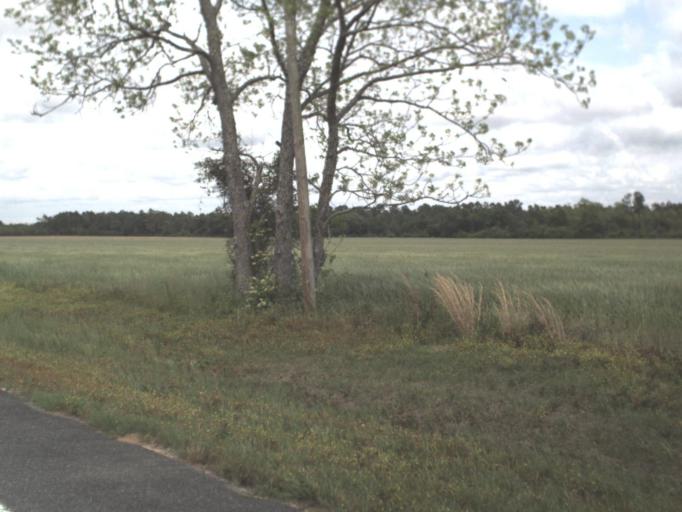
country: US
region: Florida
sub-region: Santa Rosa County
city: Point Baker
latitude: 30.7114
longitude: -87.0783
